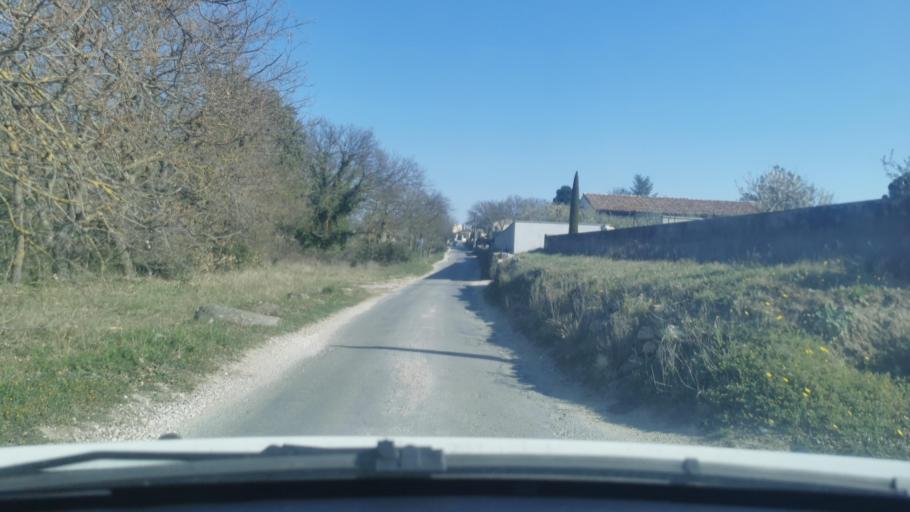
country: FR
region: Languedoc-Roussillon
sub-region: Departement du Gard
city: Montaren-et-Saint-Mediers
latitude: 44.0285
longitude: 4.3913
